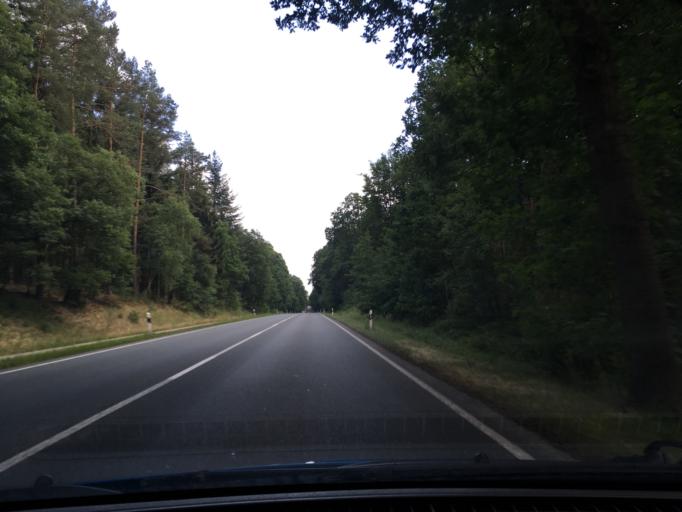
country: DE
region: Lower Saxony
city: Welle
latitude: 53.2749
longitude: 9.7987
